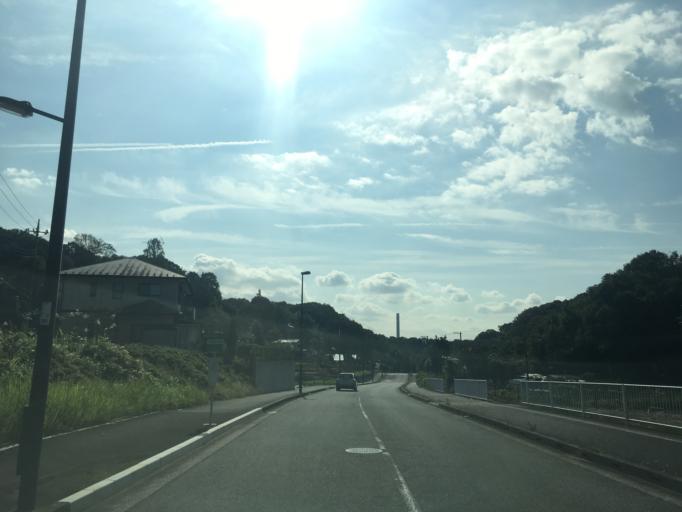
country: JP
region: Tokyo
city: Hino
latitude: 35.6019
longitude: 139.4084
